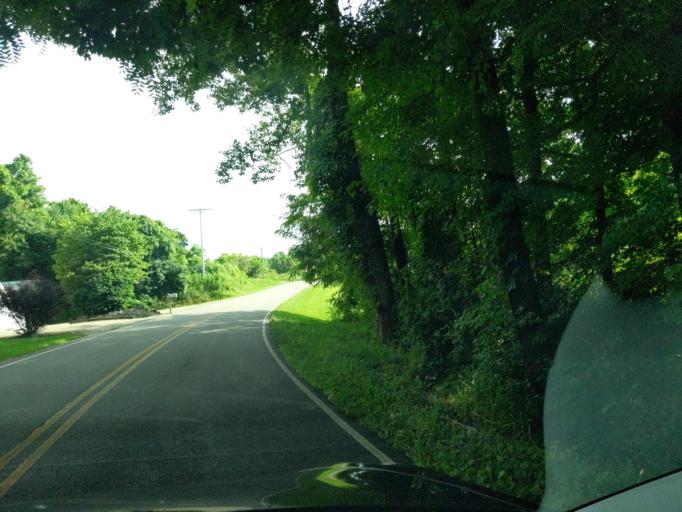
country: US
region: Ohio
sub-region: Fairfield County
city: Lancaster
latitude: 39.5508
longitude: -82.6281
